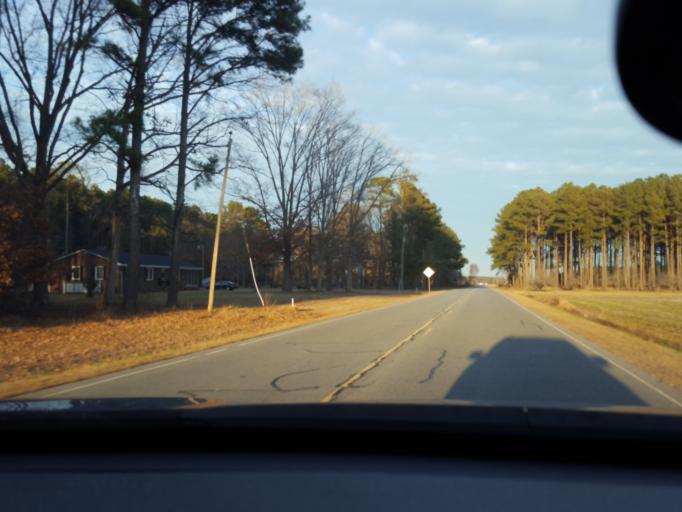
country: US
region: North Carolina
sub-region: Hertford County
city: Murfreesboro
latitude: 36.2787
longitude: -77.2032
